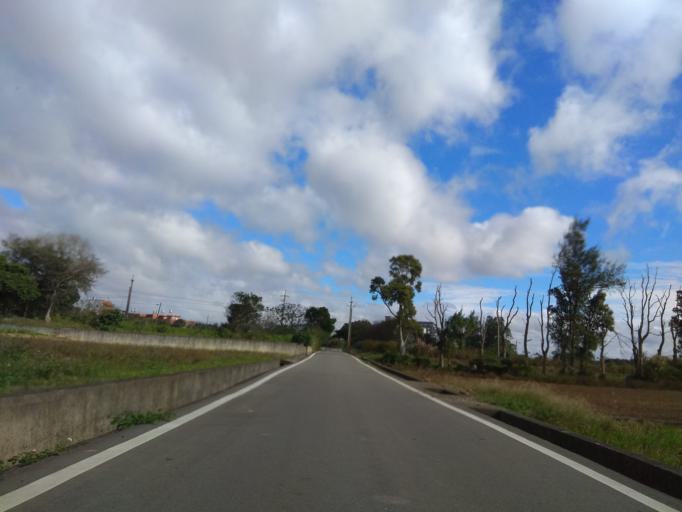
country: TW
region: Taiwan
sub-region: Hsinchu
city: Zhubei
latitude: 24.9725
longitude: 121.0851
